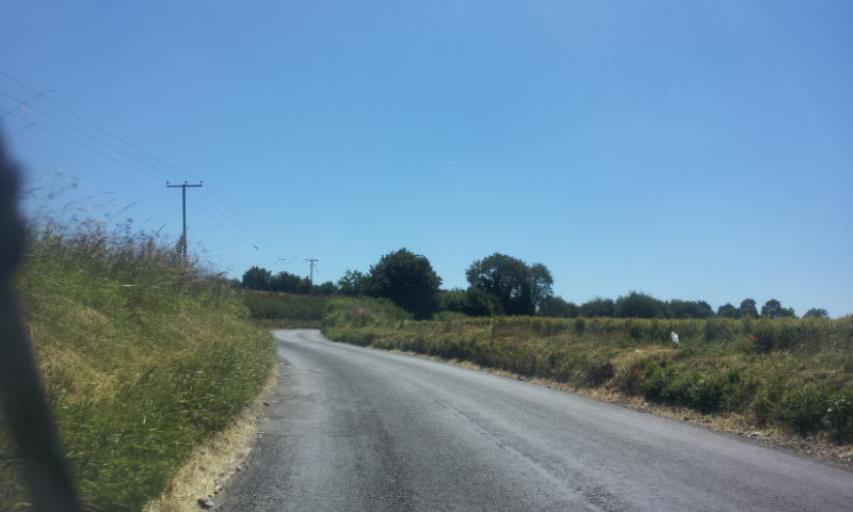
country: GB
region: England
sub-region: Kent
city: Sittingbourne
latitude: 51.3203
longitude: 0.6997
